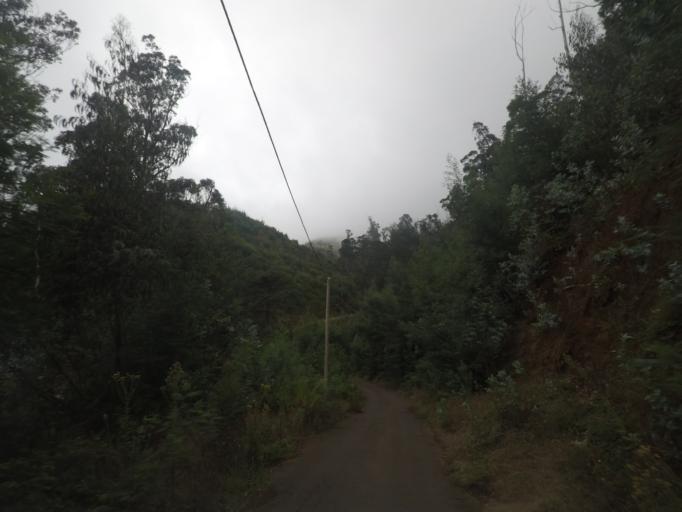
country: PT
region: Madeira
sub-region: Funchal
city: Nossa Senhora do Monte
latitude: 32.6952
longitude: -16.9081
